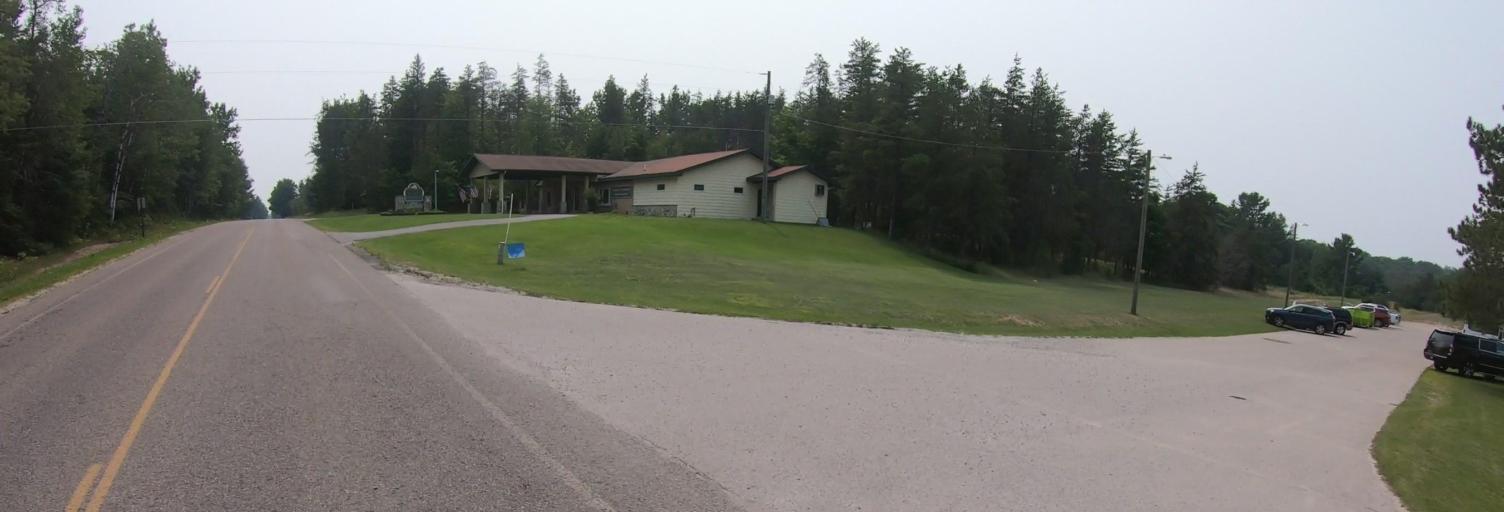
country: CA
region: Ontario
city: Thessalon
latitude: 46.0153
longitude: -83.7383
